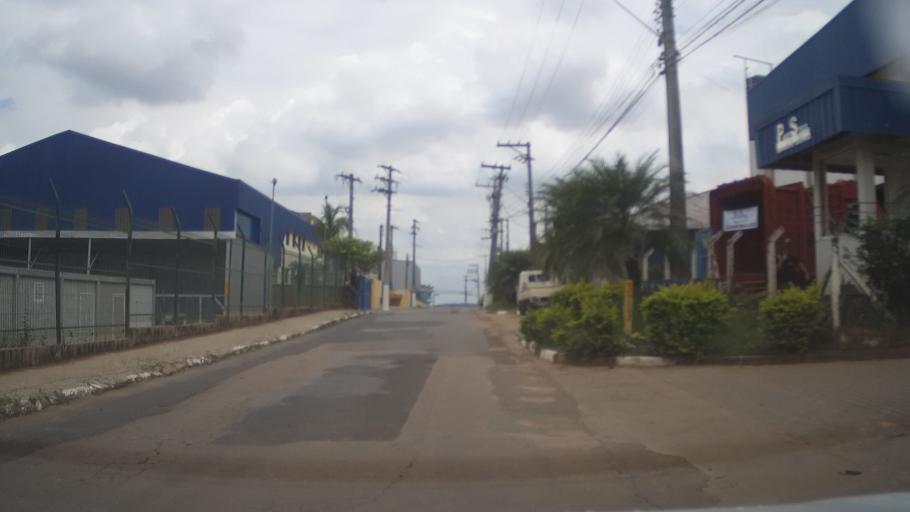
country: BR
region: Sao Paulo
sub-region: Itupeva
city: Itupeva
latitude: -23.1564
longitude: -47.0352
